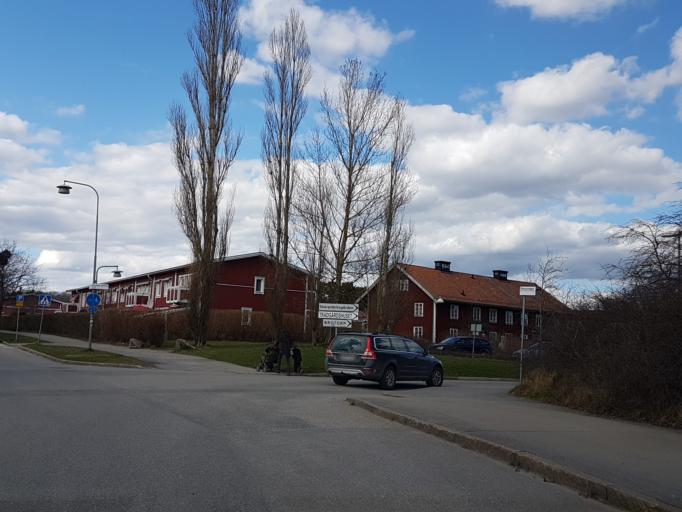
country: SE
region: Stockholm
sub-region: Nacka Kommun
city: Alta
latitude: 59.2650
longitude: 18.1426
